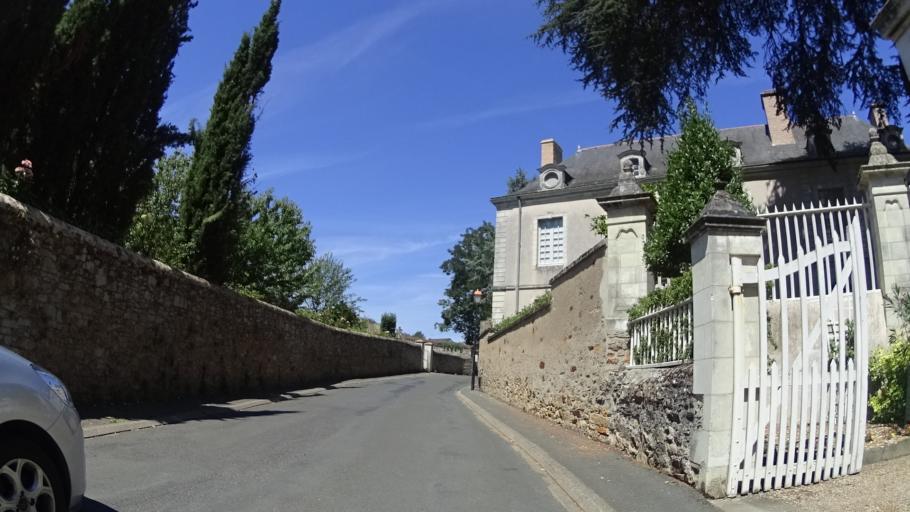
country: FR
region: Pays de la Loire
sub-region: Departement de Maine-et-Loire
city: Grez-Neuville
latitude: 47.6031
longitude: -0.6881
